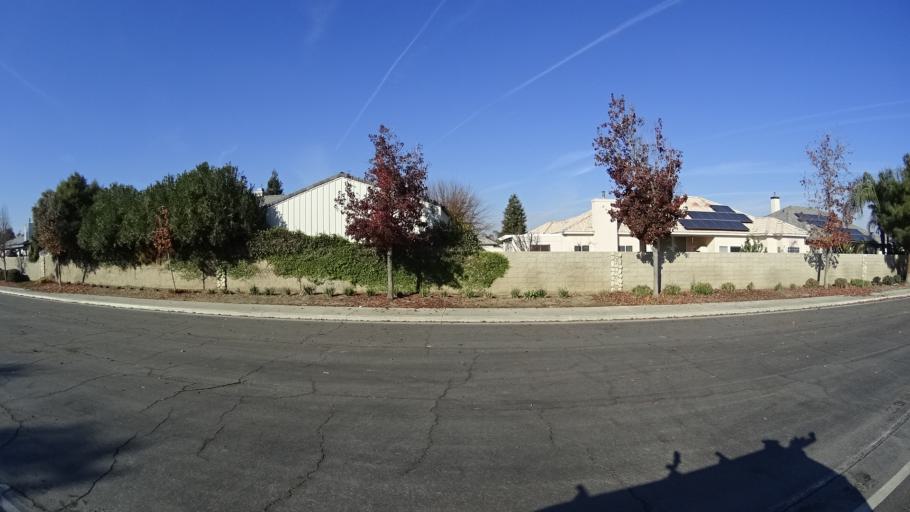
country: US
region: California
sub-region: Kern County
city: Greenfield
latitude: 35.2815
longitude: -119.0510
